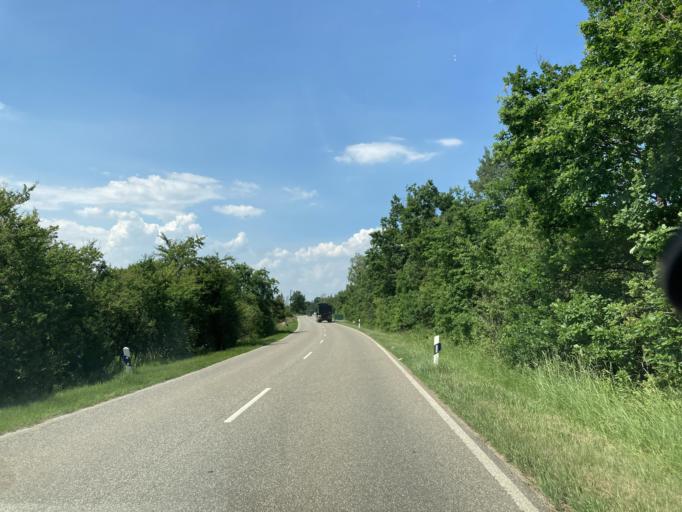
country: DE
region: Baden-Wuerttemberg
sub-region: Karlsruhe Region
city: Graben-Neudorf
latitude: 49.1843
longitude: 8.4850
